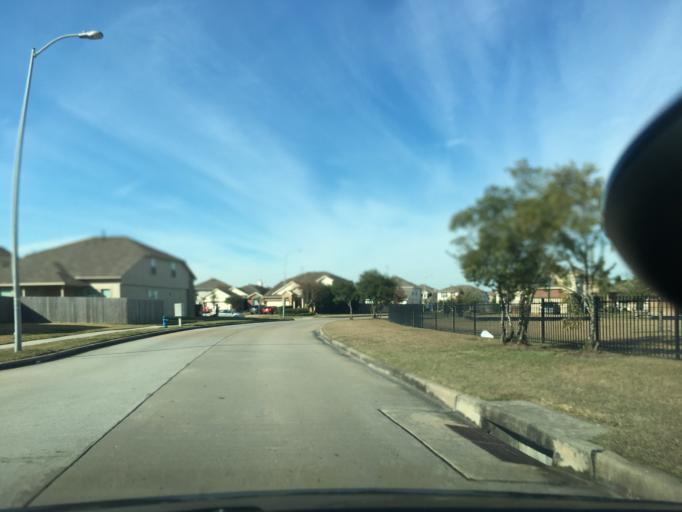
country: US
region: Texas
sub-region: Harris County
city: Cloverleaf
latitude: 29.8119
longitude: -95.1581
